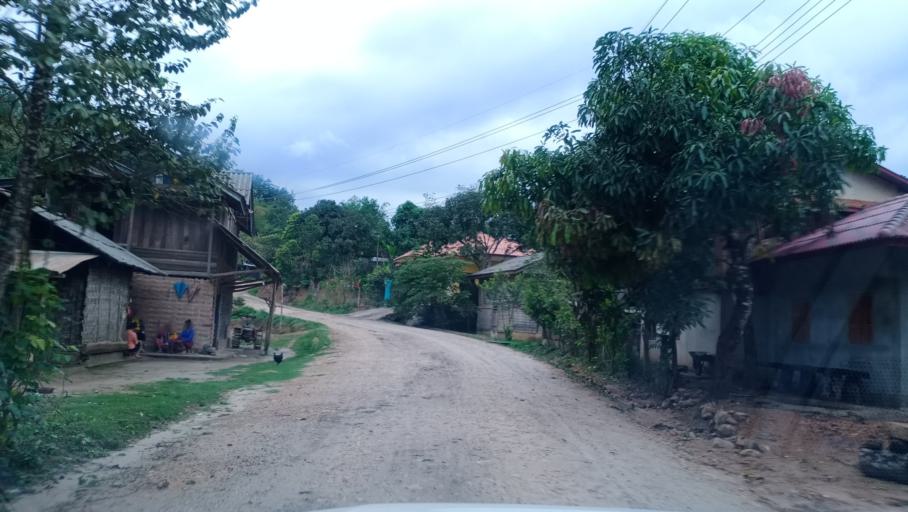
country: LA
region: Phongsali
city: Khoa
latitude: 21.1967
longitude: 102.6915
